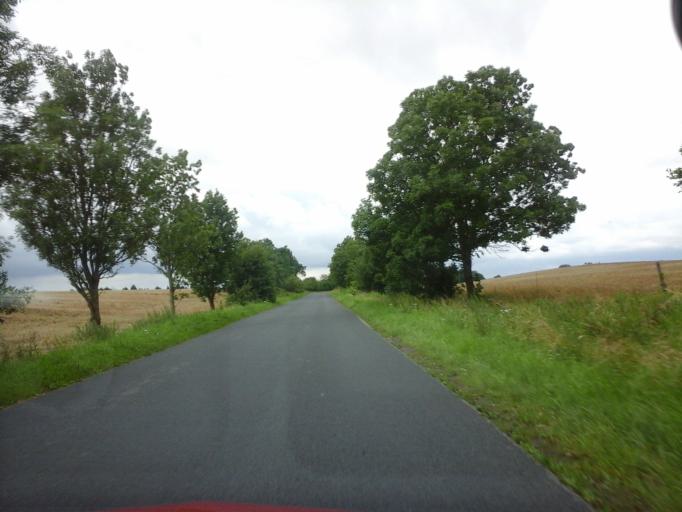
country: PL
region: West Pomeranian Voivodeship
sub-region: Powiat choszczenski
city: Bierzwnik
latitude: 53.0446
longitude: 15.6943
